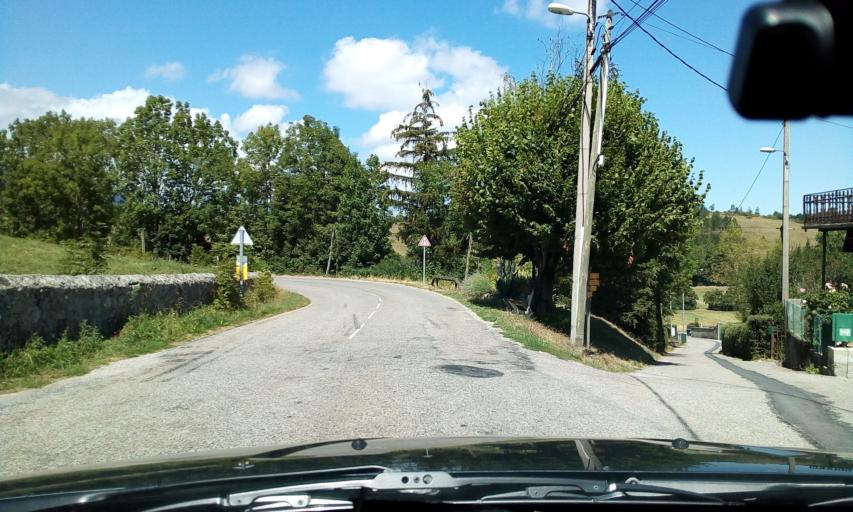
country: FR
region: Rhone-Alpes
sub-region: Departement de l'Isere
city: Mens
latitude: 44.7591
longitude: 5.6760
